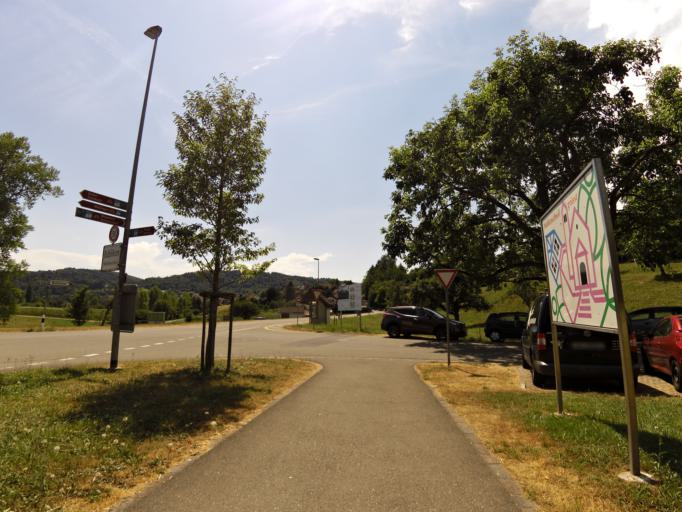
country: CH
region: Aargau
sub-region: Bezirk Baden
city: Mellingen
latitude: 47.4220
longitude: 8.2619
